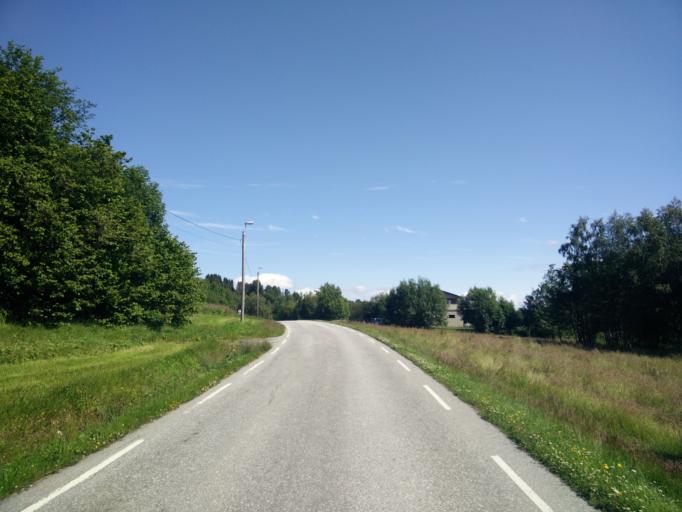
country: NO
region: More og Romsdal
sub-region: Kristiansund
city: Rensvik
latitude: 63.0466
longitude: 7.8563
